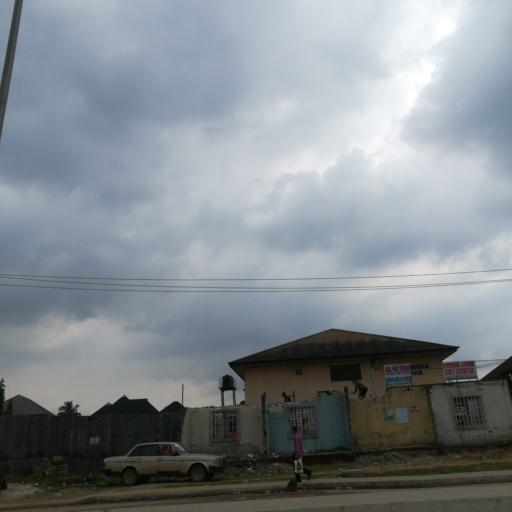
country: NG
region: Rivers
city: Port Harcourt
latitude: 4.8379
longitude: 7.0703
